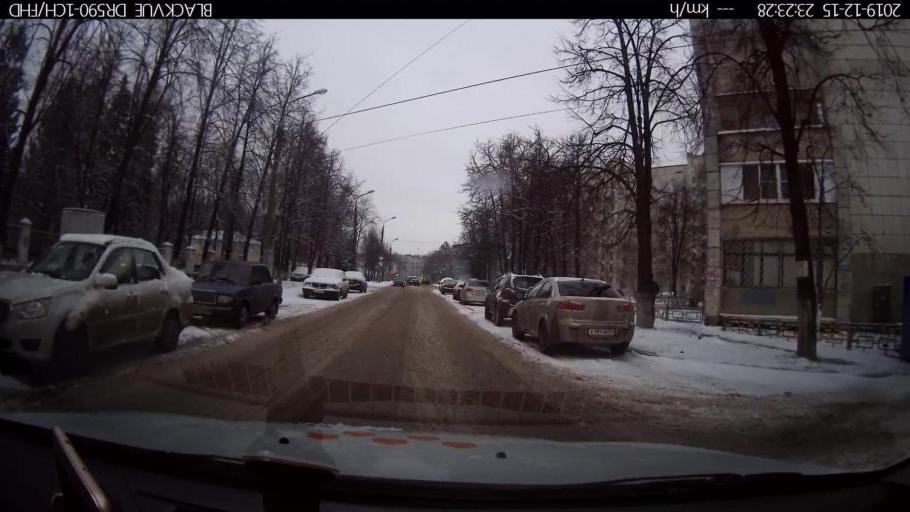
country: RU
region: Nizjnij Novgorod
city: Nizhniy Novgorod
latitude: 56.3237
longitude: 43.8739
